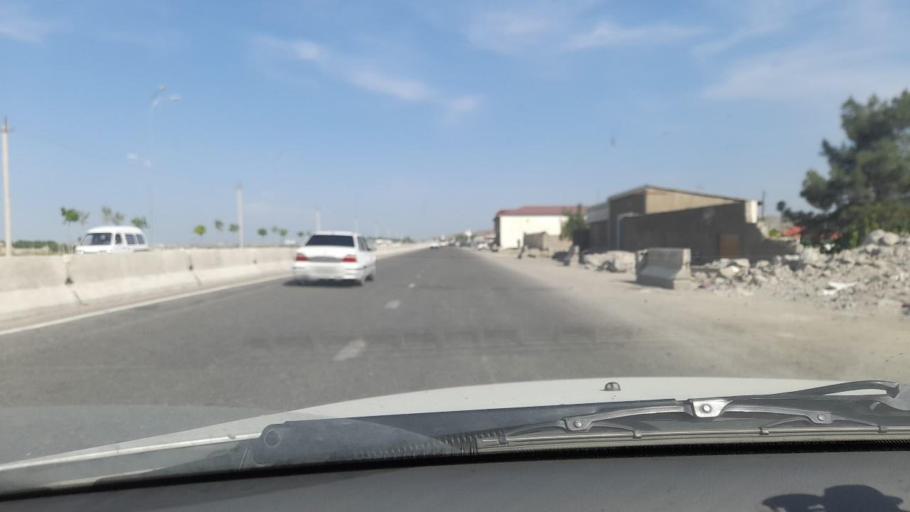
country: UZ
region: Samarqand
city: Samarqand
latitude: 39.7043
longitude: 67.0008
